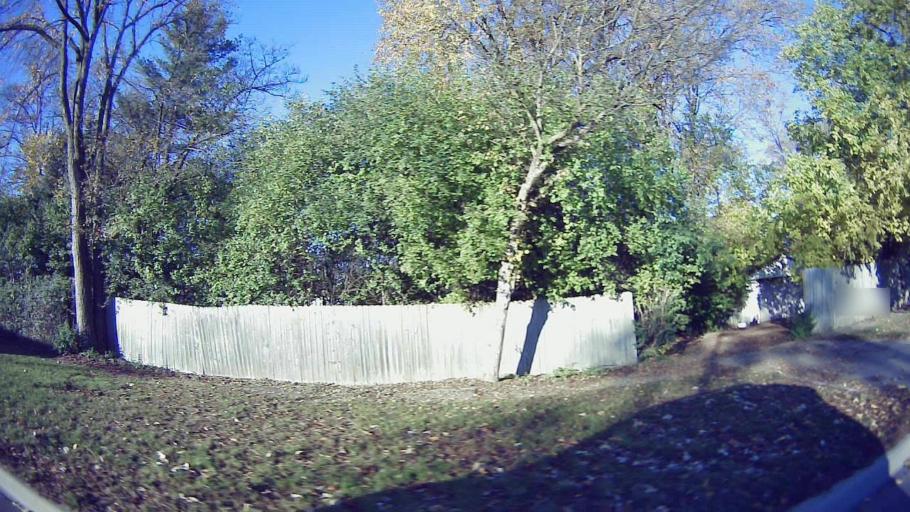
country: US
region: Michigan
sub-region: Oakland County
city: Berkley
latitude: 42.5041
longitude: -83.1841
